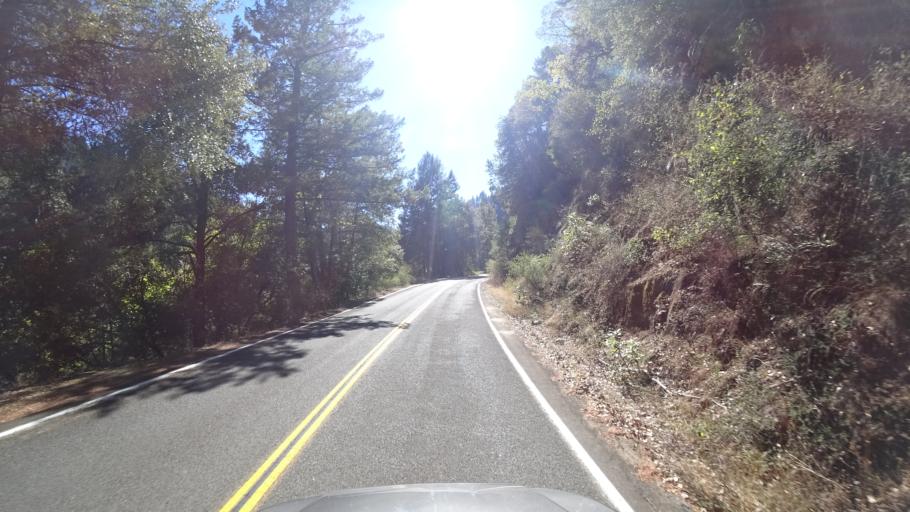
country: US
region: California
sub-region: Siskiyou County
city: Happy Camp
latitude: 41.3674
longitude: -123.4142
